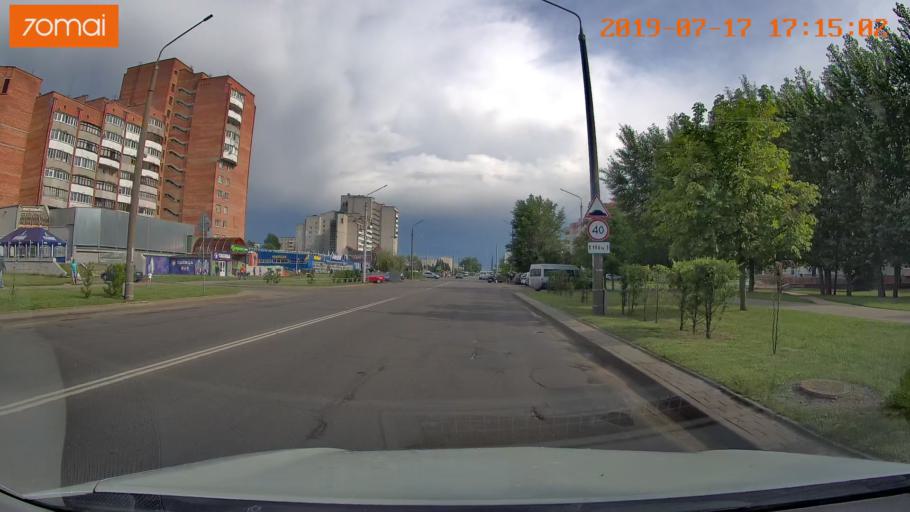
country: BY
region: Mogilev
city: Babruysk
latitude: 53.1721
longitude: 29.1897
